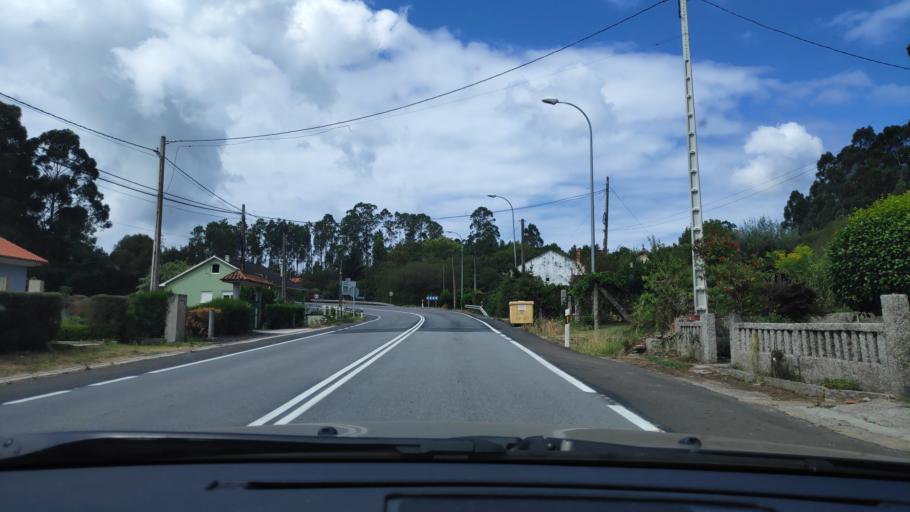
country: ES
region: Galicia
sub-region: Provincia de Pontevedra
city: Portas
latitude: 42.5779
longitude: -8.7087
